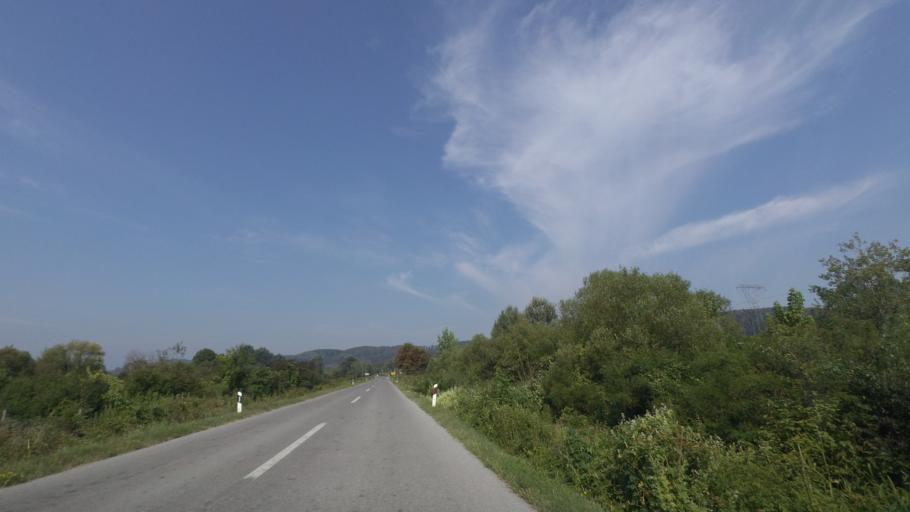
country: HR
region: Sisacko-Moslavacka
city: Hrvatska Kostajnica
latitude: 45.2298
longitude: 16.6081
